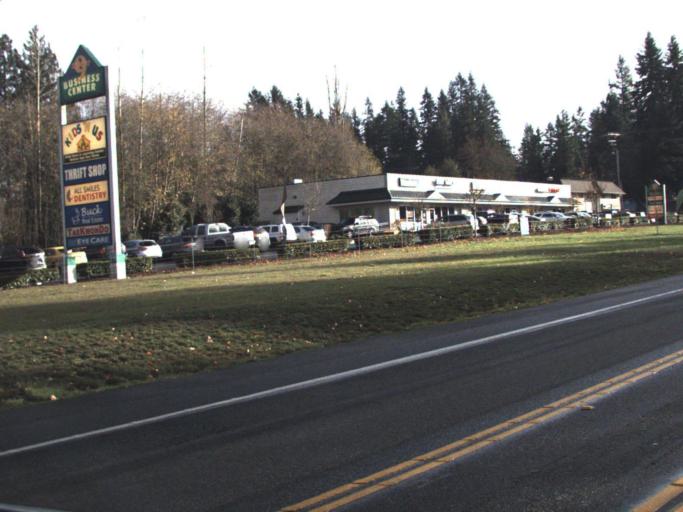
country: US
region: Washington
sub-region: Snohomish County
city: West Lake Stevens
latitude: 47.9688
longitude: -122.1023
